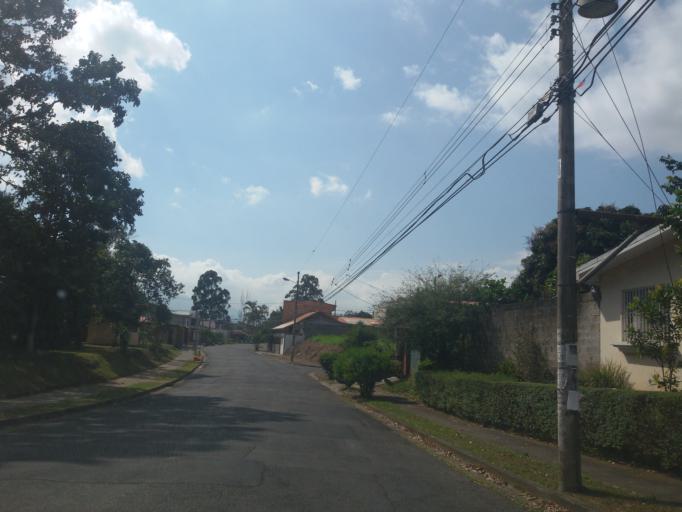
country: CR
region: San Jose
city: Curridabat
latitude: 9.9080
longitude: -84.0341
